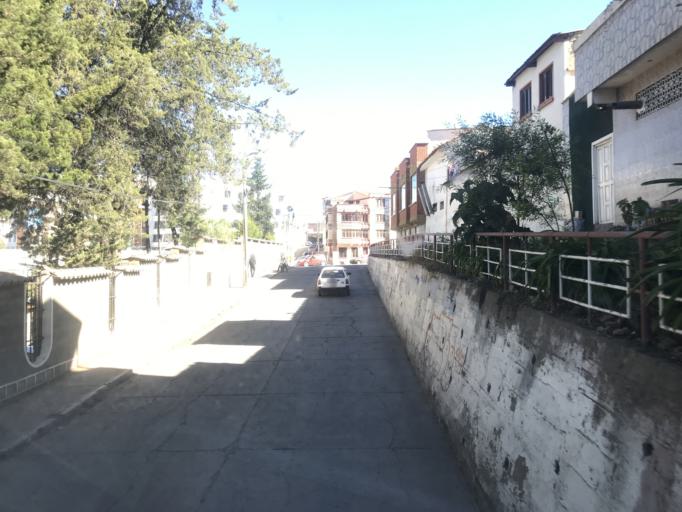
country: BO
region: Chuquisaca
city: Sucre
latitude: -19.0420
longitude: -65.2475
